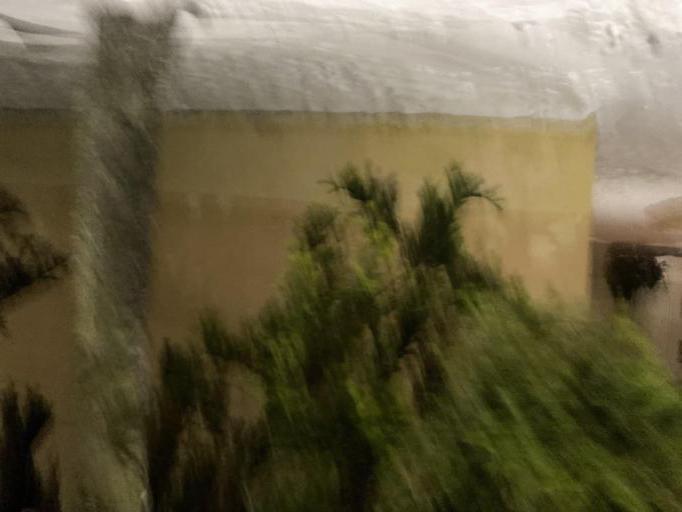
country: LV
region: Ludzas Rajons
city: Ludza
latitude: 56.5404
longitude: 27.7169
